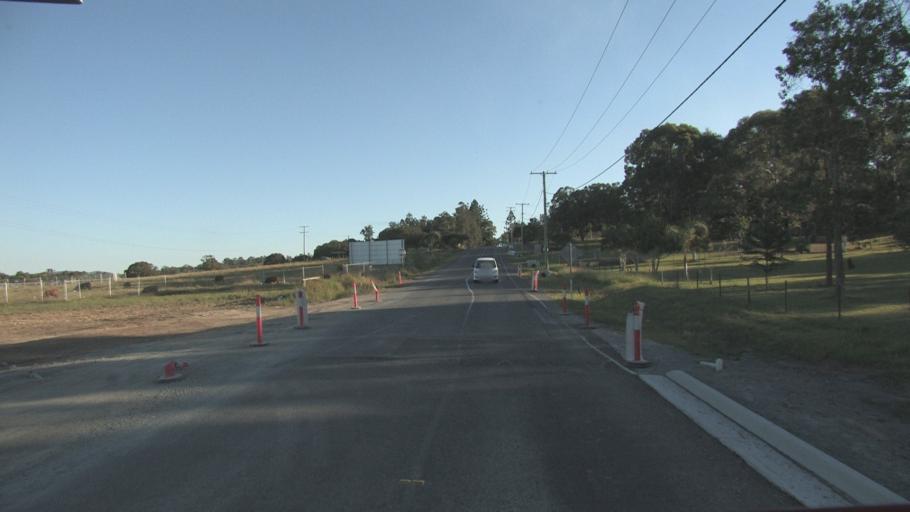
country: AU
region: Queensland
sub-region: Logan
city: Logan Reserve
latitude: -27.7173
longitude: 153.1146
